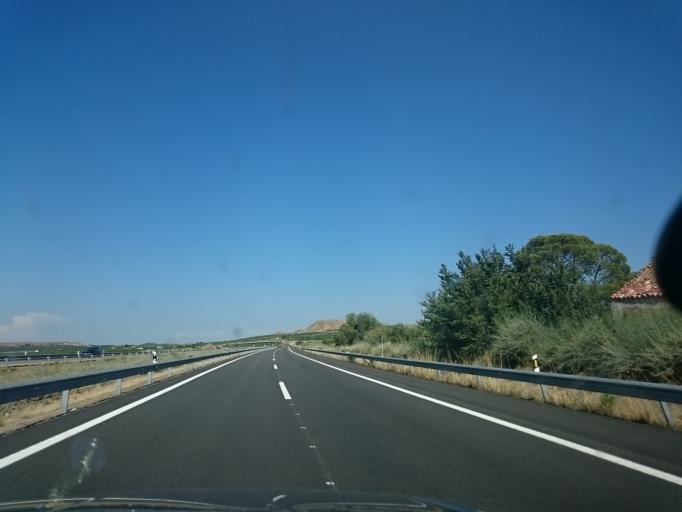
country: ES
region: Catalonia
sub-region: Provincia de Lleida
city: Seros
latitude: 41.5077
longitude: 0.4175
